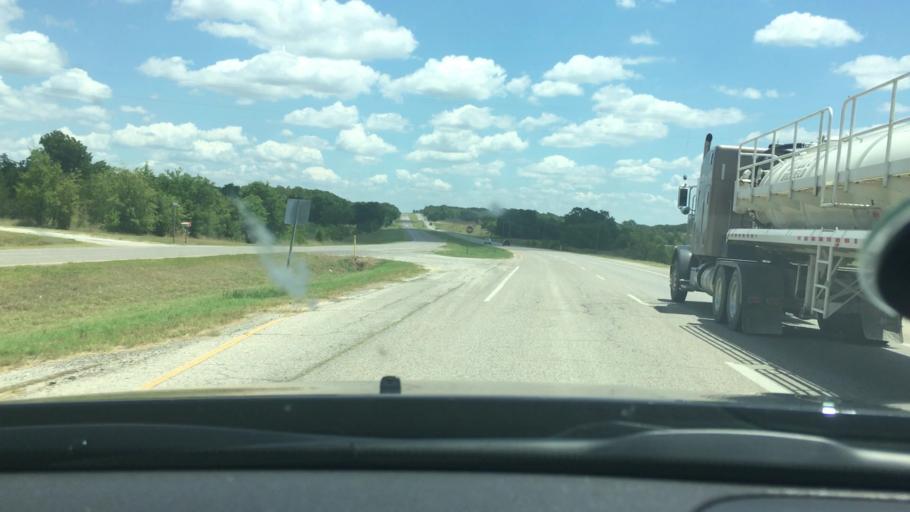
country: US
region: Oklahoma
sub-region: Carter County
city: Wilson
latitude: 34.1730
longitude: -97.3627
